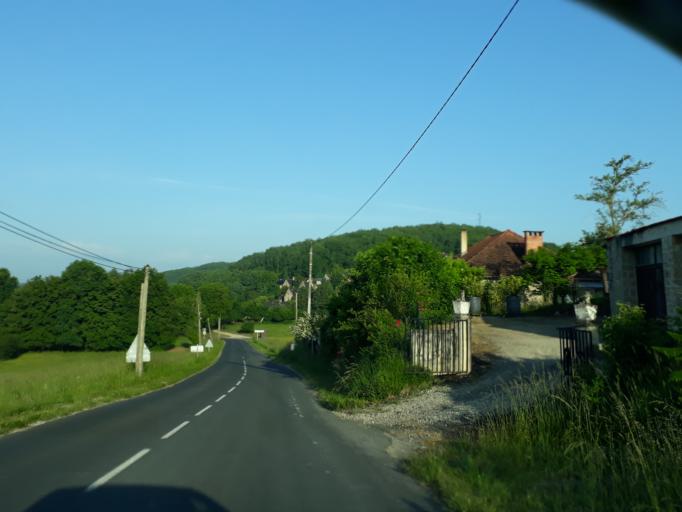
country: FR
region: Limousin
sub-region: Departement de la Correze
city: Saint-Pantaleon-de-Larche
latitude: 45.1051
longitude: 1.4668
